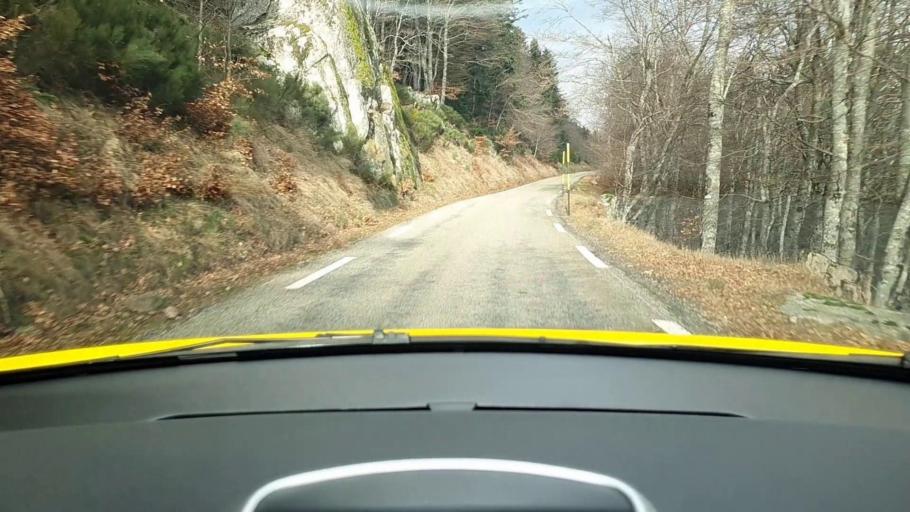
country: FR
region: Languedoc-Roussillon
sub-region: Departement du Gard
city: Branoux-les-Taillades
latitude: 44.3624
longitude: 3.9170
